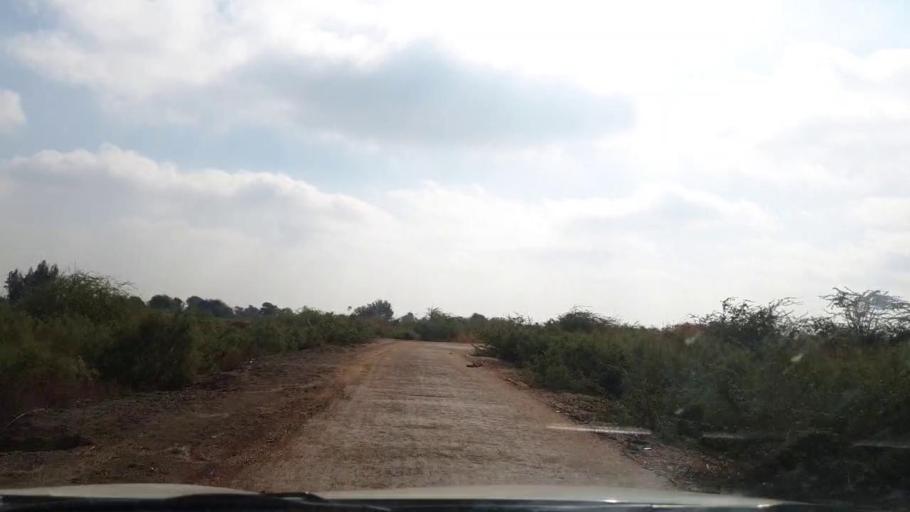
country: PK
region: Sindh
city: Berani
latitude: 25.7814
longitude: 68.9679
